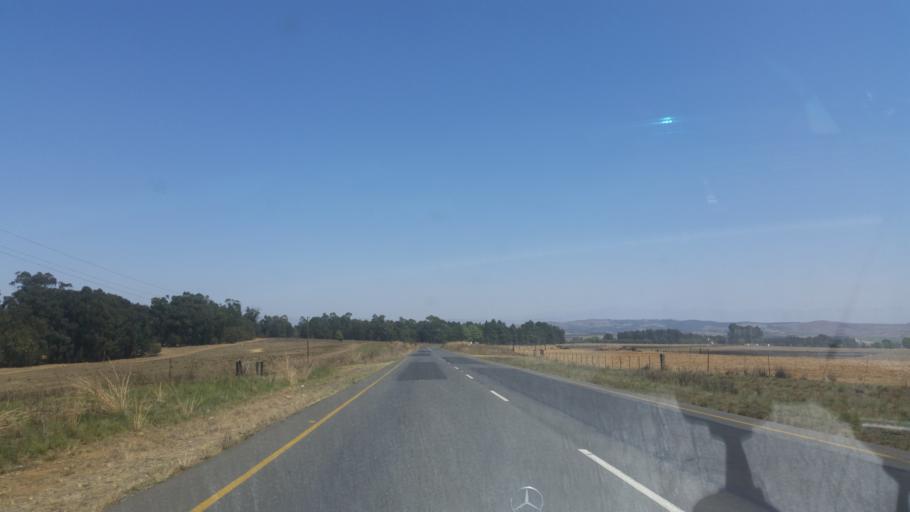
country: ZA
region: KwaZulu-Natal
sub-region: uMgungundlovu District Municipality
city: Mooirivier
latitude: -29.1466
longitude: 29.9892
